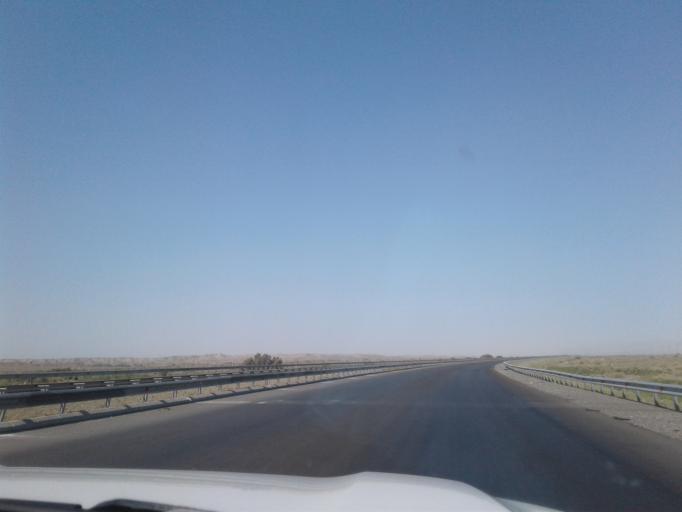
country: TM
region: Balkan
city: Gazanjyk
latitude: 39.2542
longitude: 55.3751
